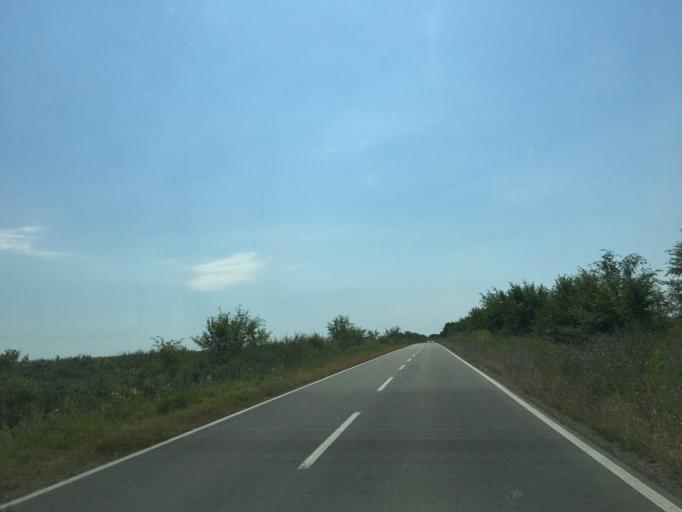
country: RS
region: Central Serbia
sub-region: Belgrade
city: Grocka
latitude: 44.7446
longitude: 20.7640
